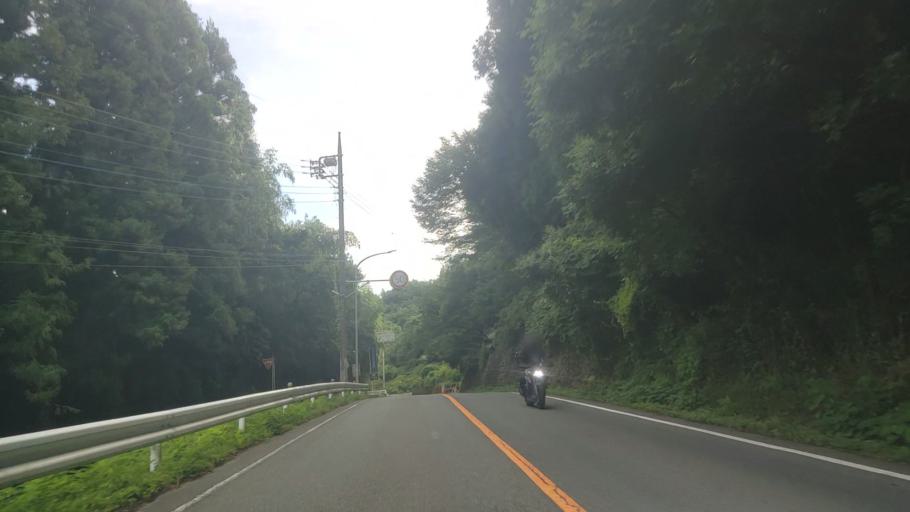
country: JP
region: Gunma
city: Omamacho-omama
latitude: 36.5201
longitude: 139.3040
